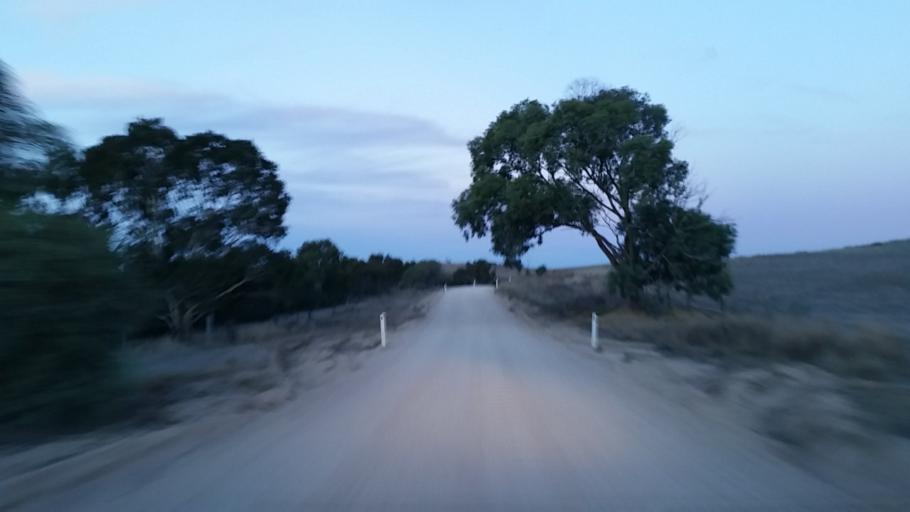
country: AU
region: South Australia
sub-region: Mount Barker
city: Callington
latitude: -35.0987
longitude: 138.9952
